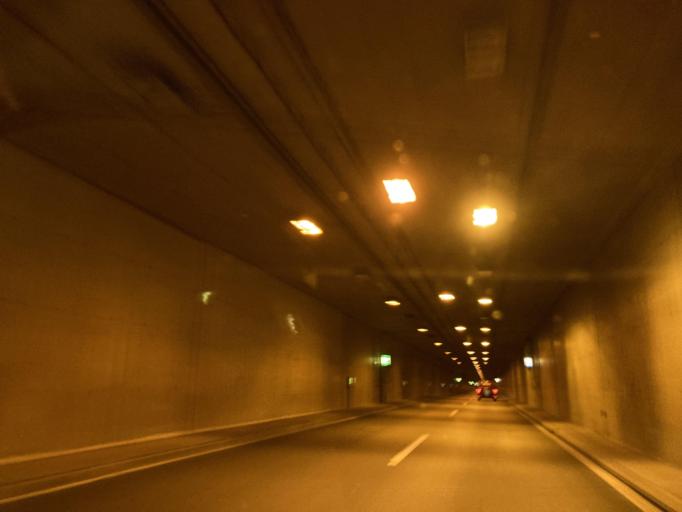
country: DE
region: Baden-Wuerttemberg
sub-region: Freiburg Region
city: Freiburg
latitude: 47.9823
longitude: 7.8938
